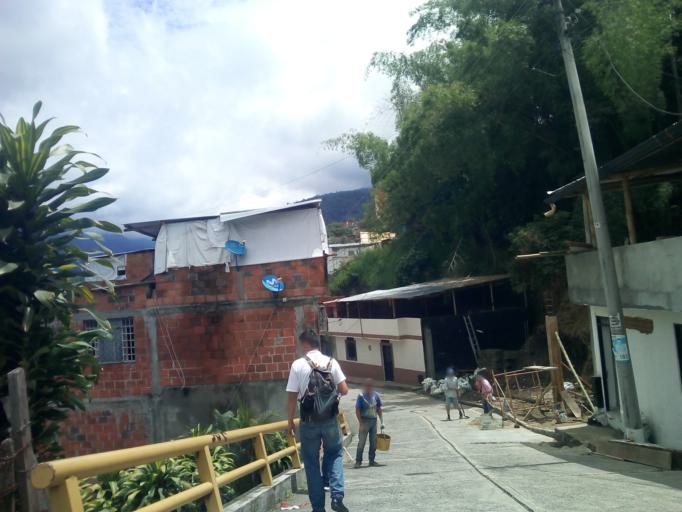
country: CO
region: Tolima
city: Ibague
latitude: 4.4471
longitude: -75.2470
